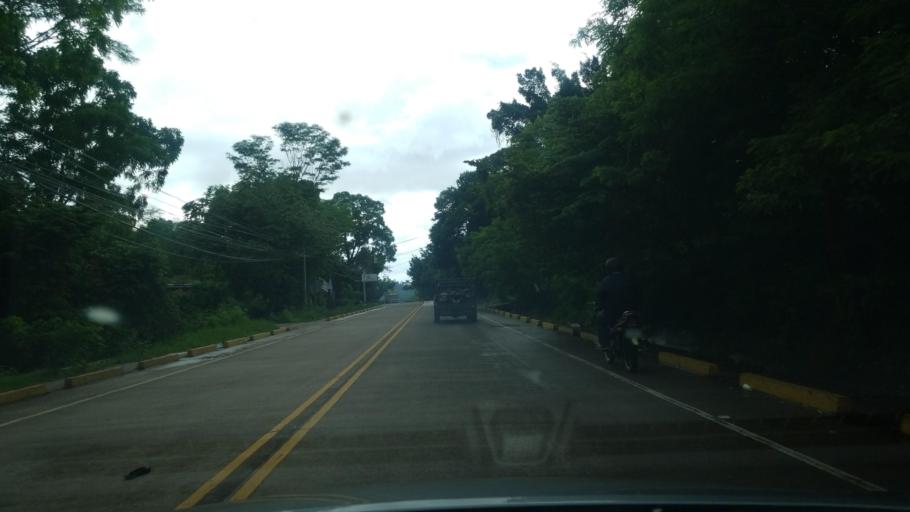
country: HN
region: Copan
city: Copan
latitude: 14.8421
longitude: -89.1655
